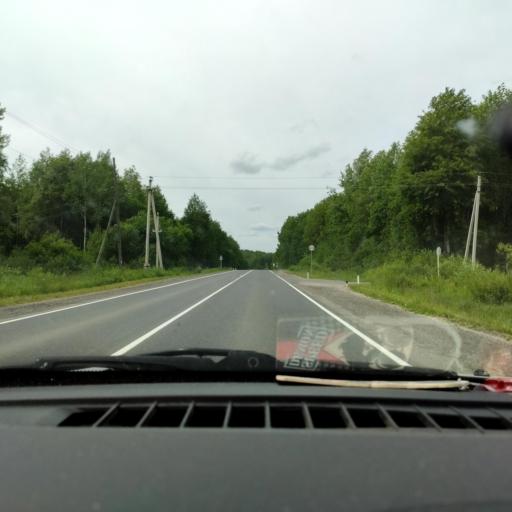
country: RU
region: Perm
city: Chusovoy
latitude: 58.3798
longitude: 57.9391
